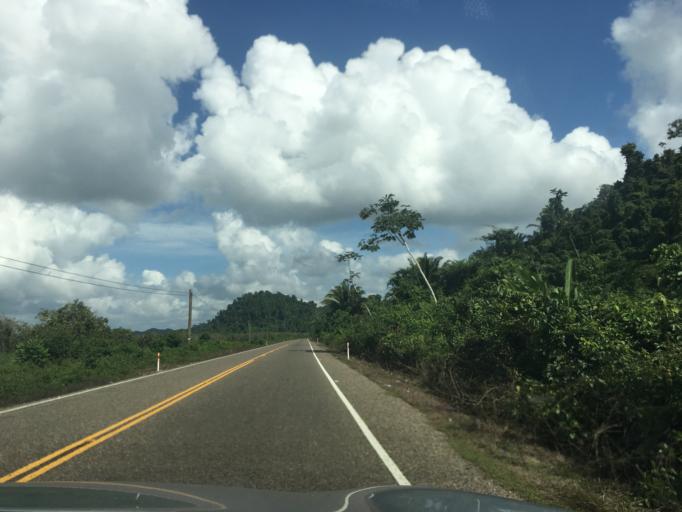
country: BZ
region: Cayo
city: Belmopan
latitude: 17.1513
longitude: -88.6938
